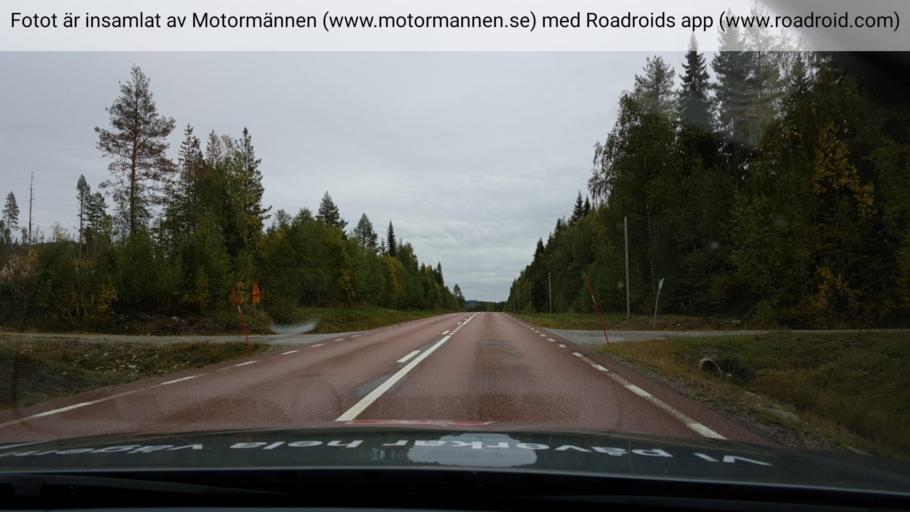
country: SE
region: Vaesterbotten
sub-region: Dorotea Kommun
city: Dorotea
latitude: 64.2055
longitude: 16.2858
